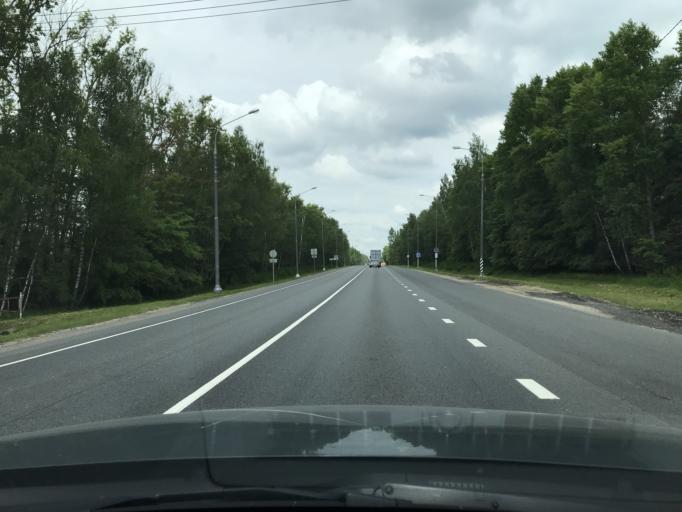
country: RU
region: Moskovskaya
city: Dorokhovo
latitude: 55.3769
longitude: 36.4053
